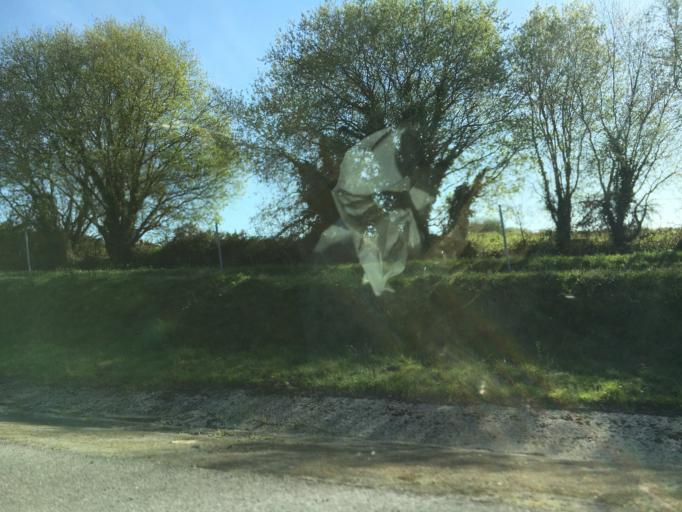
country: ES
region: Galicia
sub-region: Provincia da Coruna
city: Betanzos
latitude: 43.2729
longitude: -8.2501
